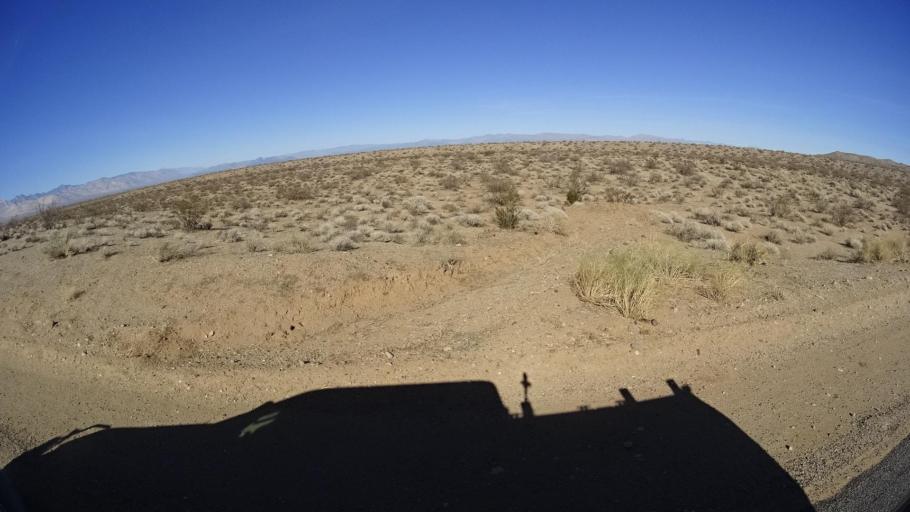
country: US
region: California
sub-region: Kern County
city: China Lake Acres
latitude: 35.5562
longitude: -117.7474
